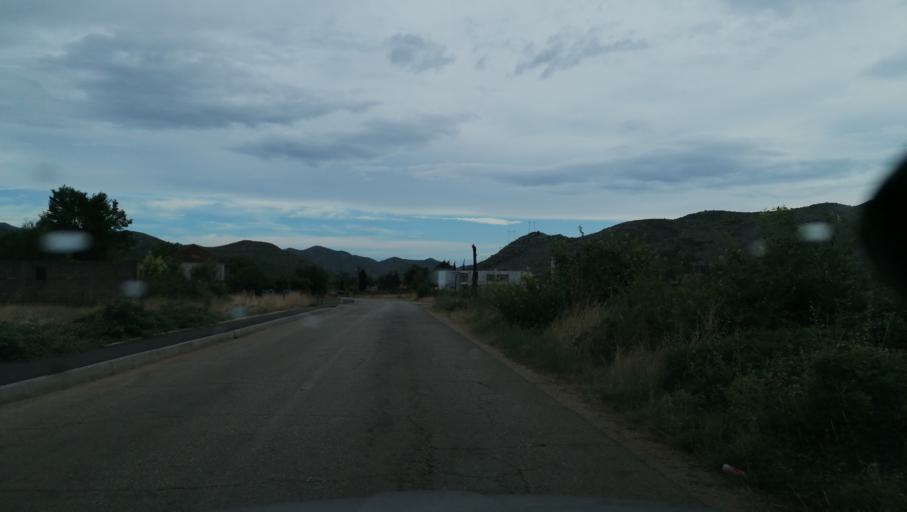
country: BA
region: Republika Srpska
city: Trebinje
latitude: 42.6729
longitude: 18.3294
